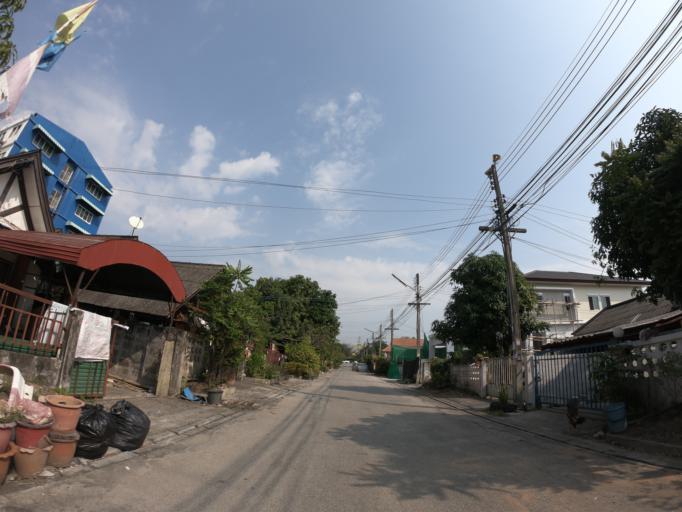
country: TH
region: Chiang Mai
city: Chiang Mai
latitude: 18.7611
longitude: 98.9942
